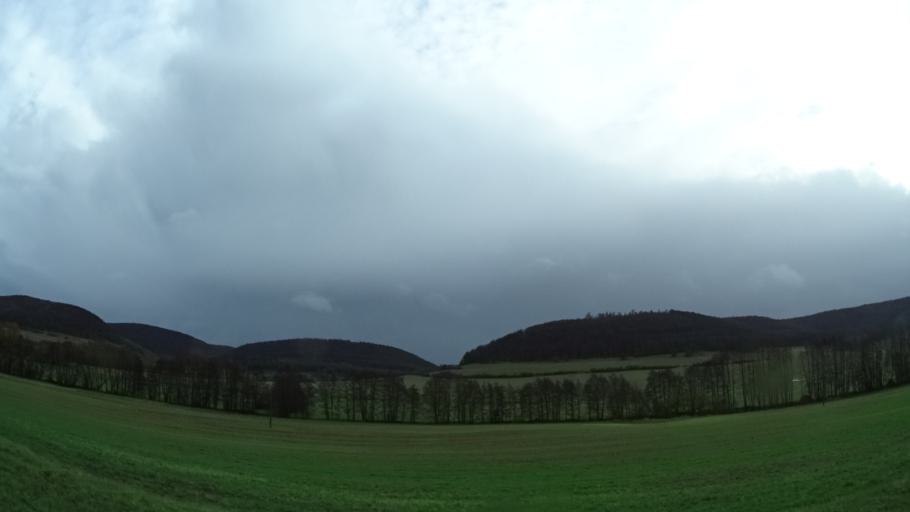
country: DE
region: Thuringia
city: Stepfershausen
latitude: 50.5714
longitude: 10.3241
